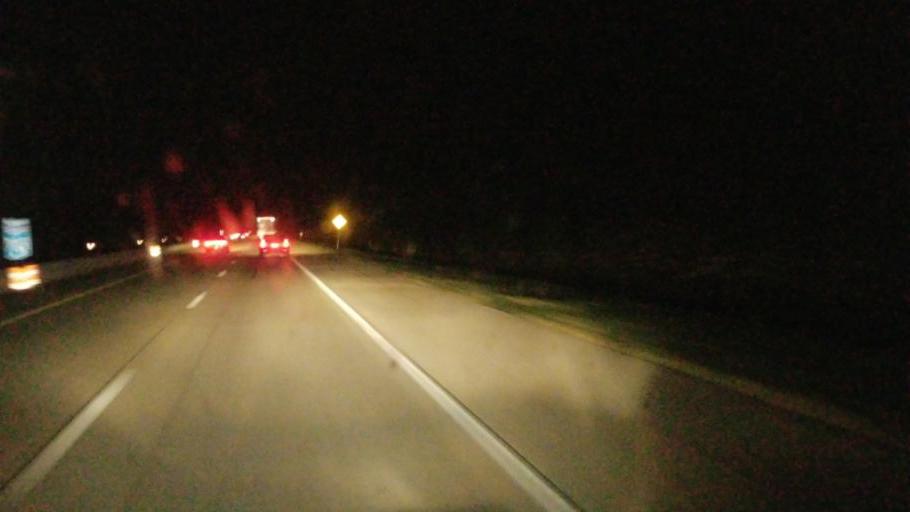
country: US
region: Indiana
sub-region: Allen County
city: Leo-Cedarville
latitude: 41.1456
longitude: -85.0148
